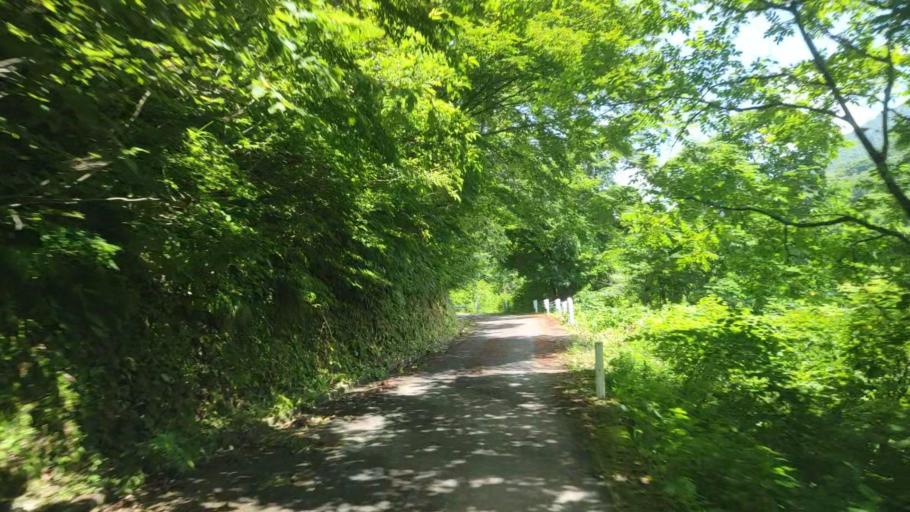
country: JP
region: Fukui
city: Ono
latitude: 35.7972
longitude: 136.4924
